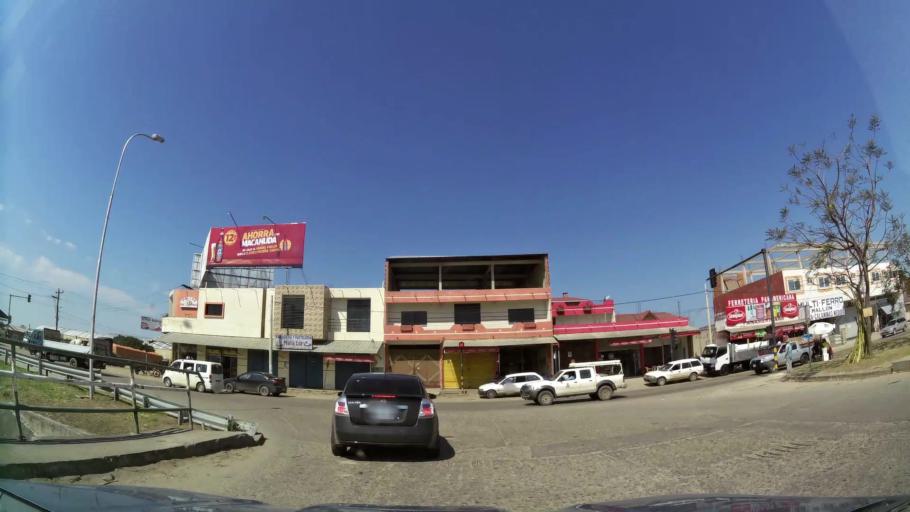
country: BO
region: Santa Cruz
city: Santa Cruz de la Sierra
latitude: -17.7430
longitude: -63.1452
